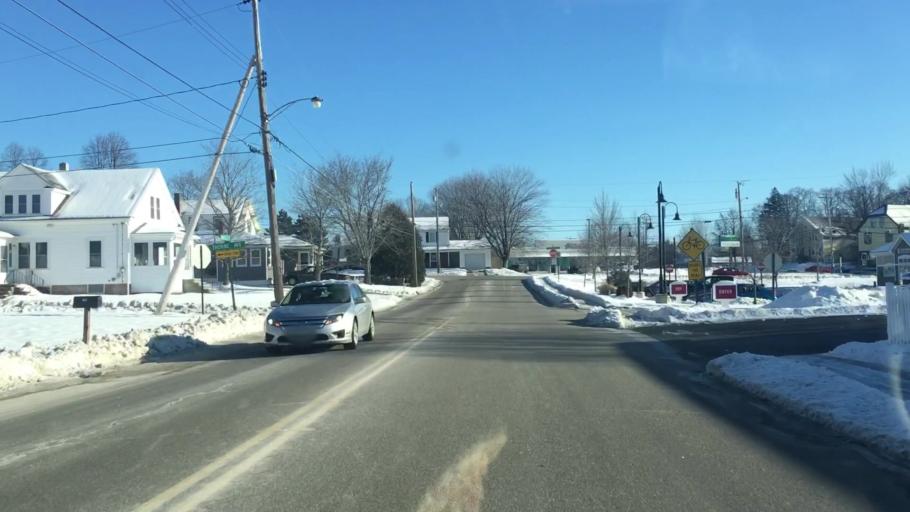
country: US
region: Maine
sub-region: Androscoggin County
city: Lewiston
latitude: 44.1043
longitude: -70.1746
